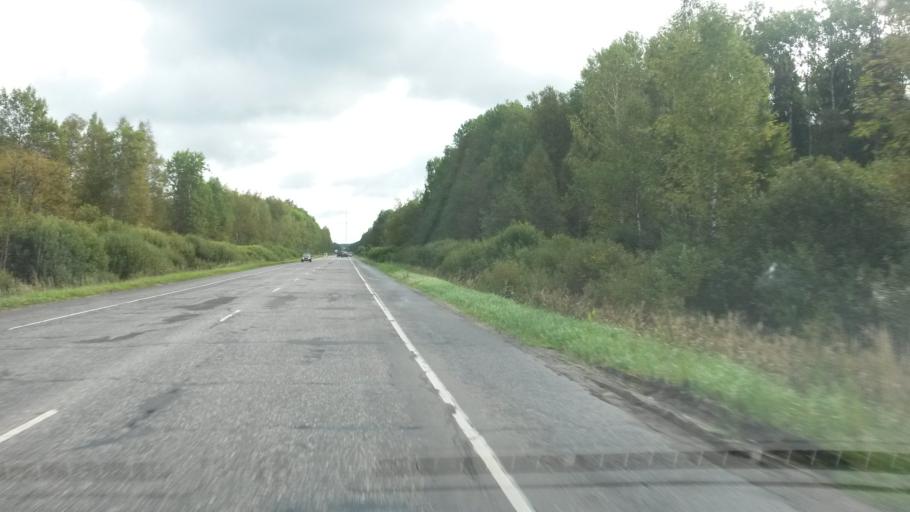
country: RU
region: Ivanovo
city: Rodniki
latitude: 57.0855
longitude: 41.5994
